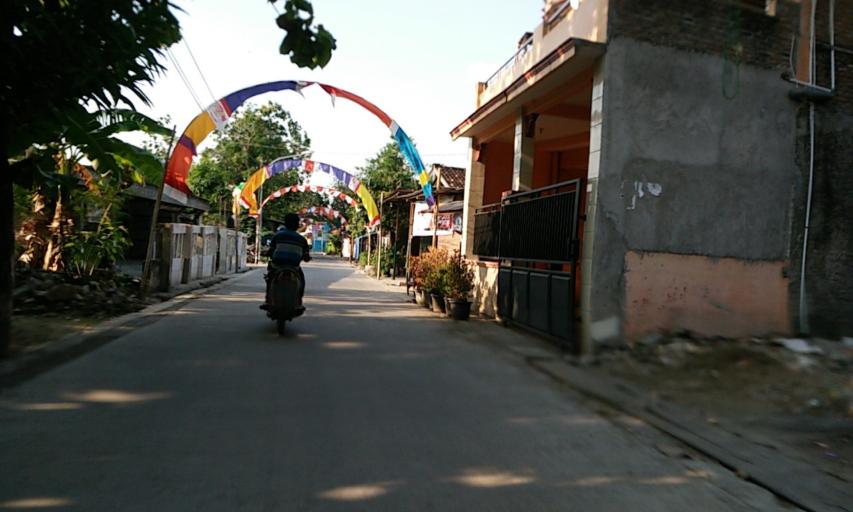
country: ID
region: Central Java
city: Mranggen
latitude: -7.0159
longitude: 110.4884
